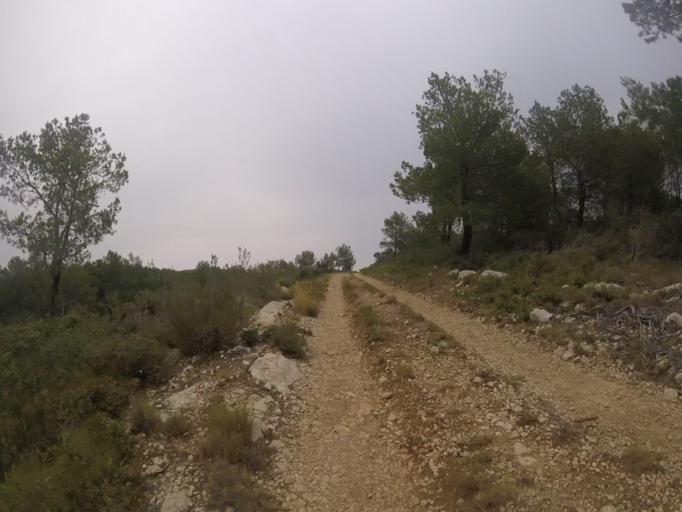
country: ES
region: Valencia
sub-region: Provincia de Castello
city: Alcoceber
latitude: 40.2843
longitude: 0.2844
